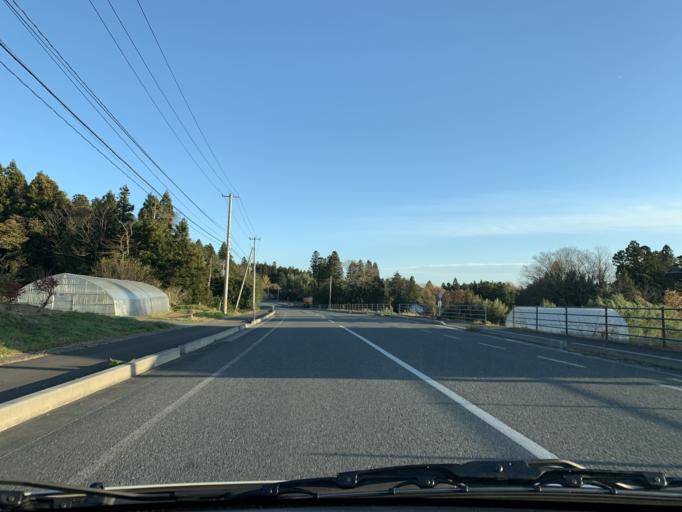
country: JP
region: Iwate
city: Ichinoseki
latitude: 38.9817
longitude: 141.1520
